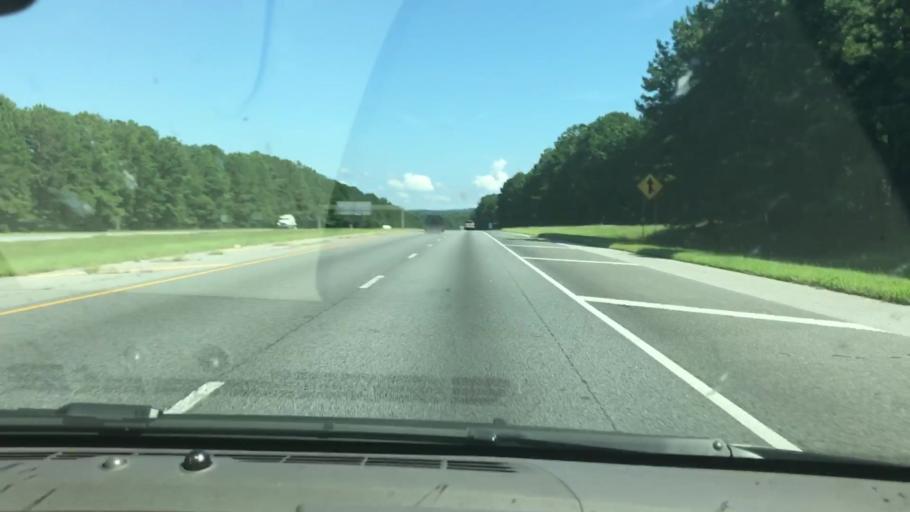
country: US
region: Alabama
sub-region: Russell County
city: Phenix City
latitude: 32.5697
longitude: -84.9618
